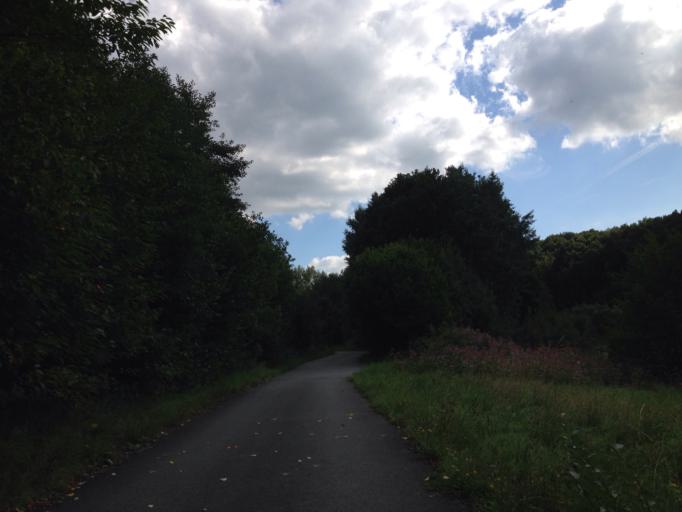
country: DE
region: Hesse
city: Hatzfeld
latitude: 50.9983
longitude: 8.5876
